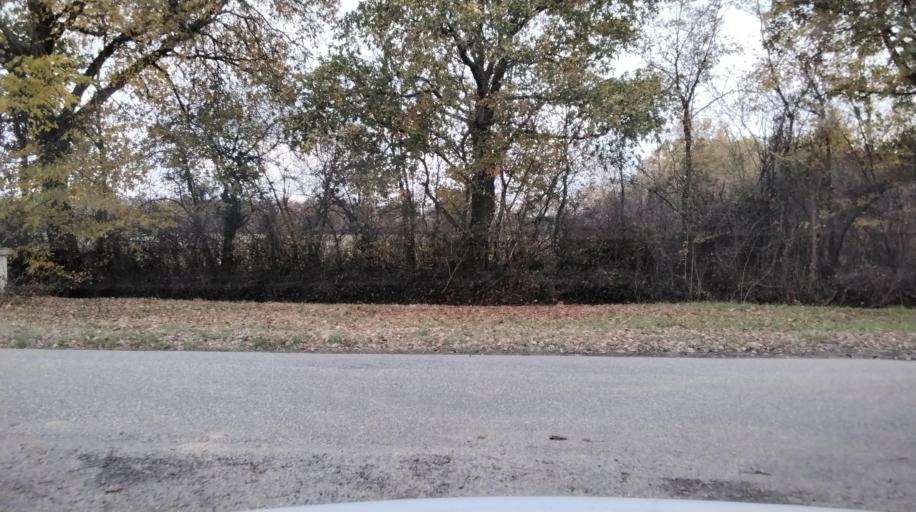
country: FR
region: Midi-Pyrenees
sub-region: Departement de la Haute-Garonne
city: Le Fousseret
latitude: 43.2666
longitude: 1.0207
